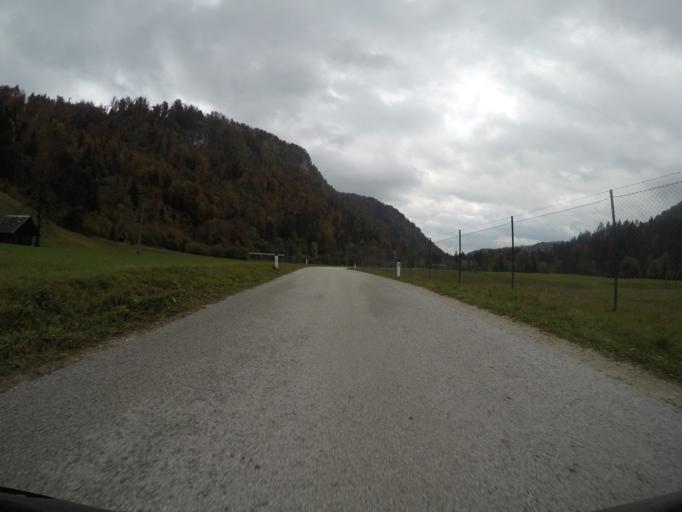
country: SI
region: Gorje
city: Zgornje Gorje
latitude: 46.3842
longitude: 14.0403
